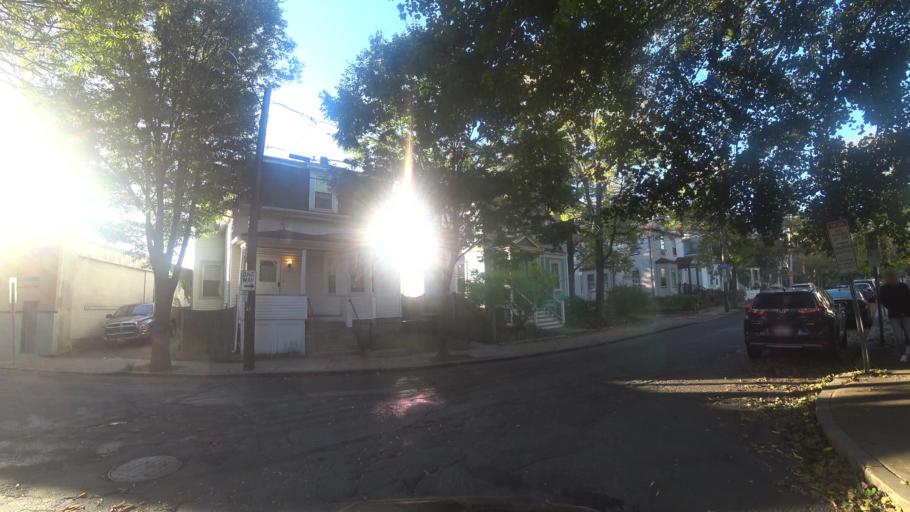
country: US
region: Massachusetts
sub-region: Middlesex County
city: Somerville
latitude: 42.3972
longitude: -71.1247
